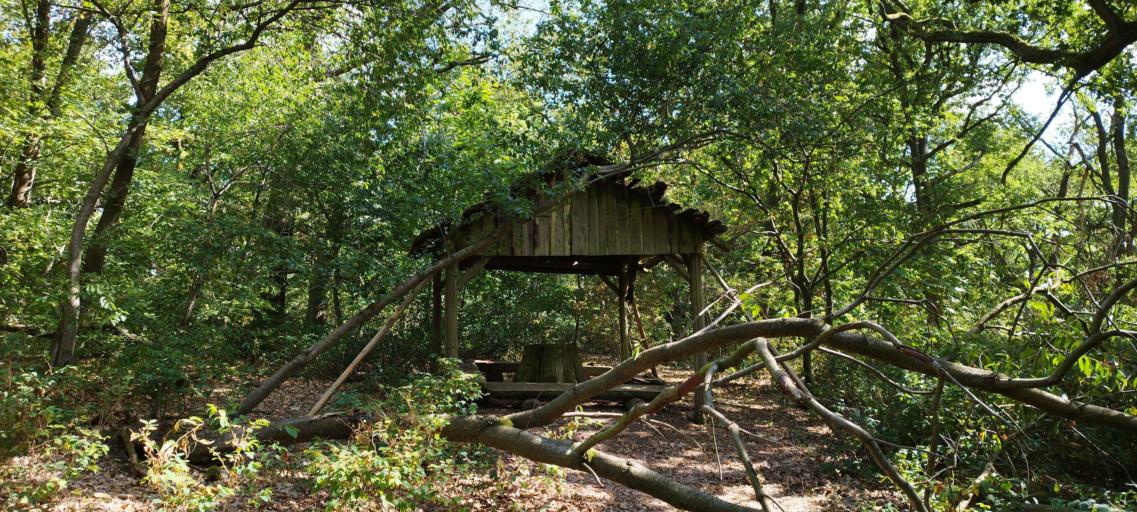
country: DE
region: Brandenburg
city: Nennhausen
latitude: 52.5977
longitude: 12.4247
